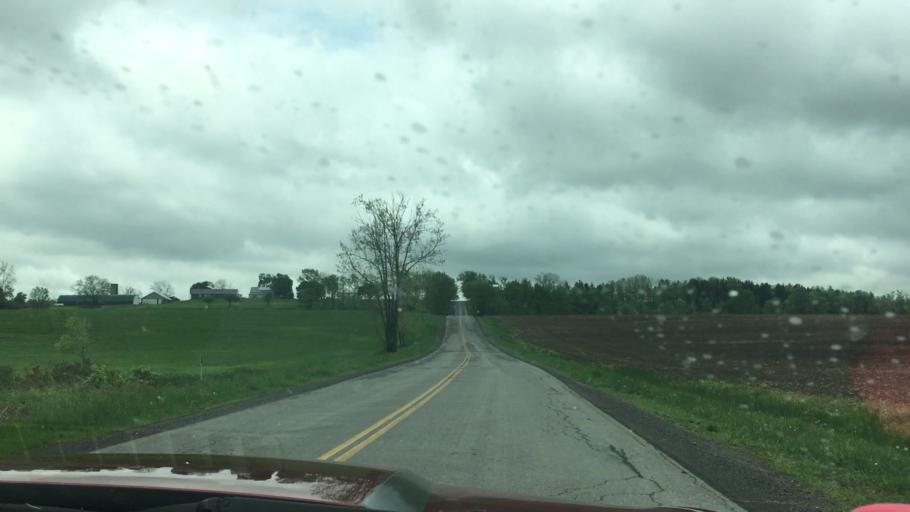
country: US
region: New York
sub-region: Genesee County
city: Batavia
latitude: 43.0891
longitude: -78.1393
